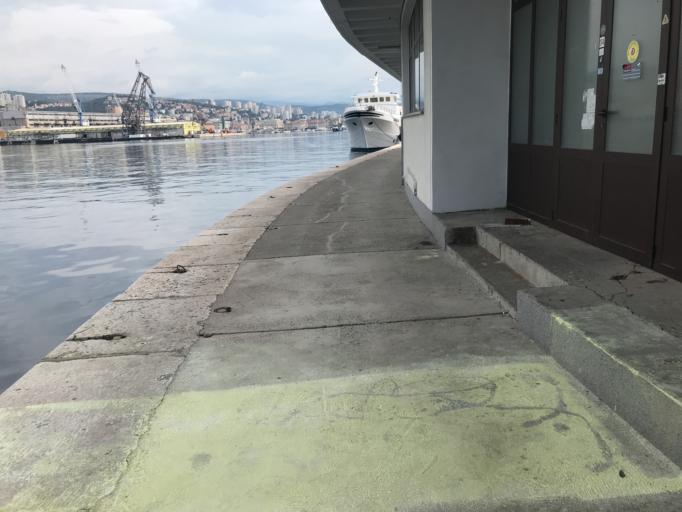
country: HR
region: Primorsko-Goranska
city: Rijeka
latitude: 45.3267
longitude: 14.4254
